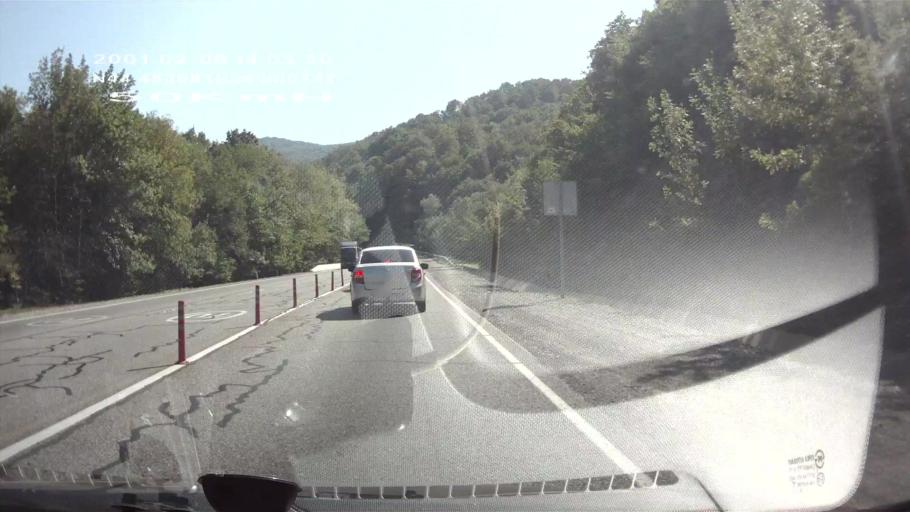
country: RU
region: Krasnodarskiy
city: Novomikhaylovskiy
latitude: 44.4834
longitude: 38.9008
